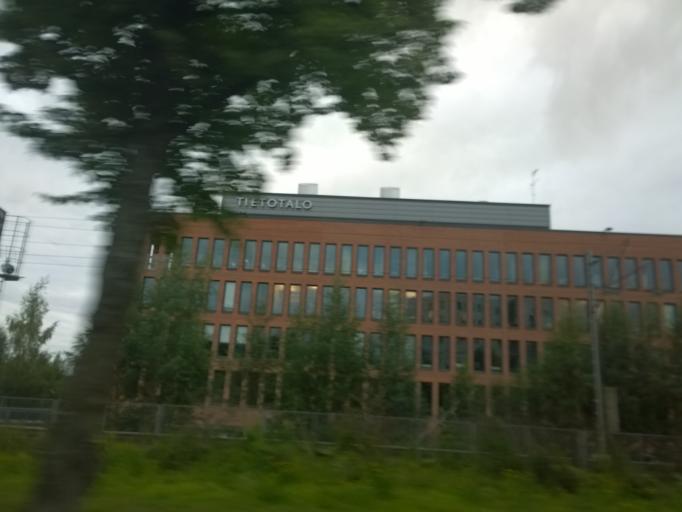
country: FI
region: Pirkanmaa
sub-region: Tampere
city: Tampere
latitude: 61.4920
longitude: 23.7789
